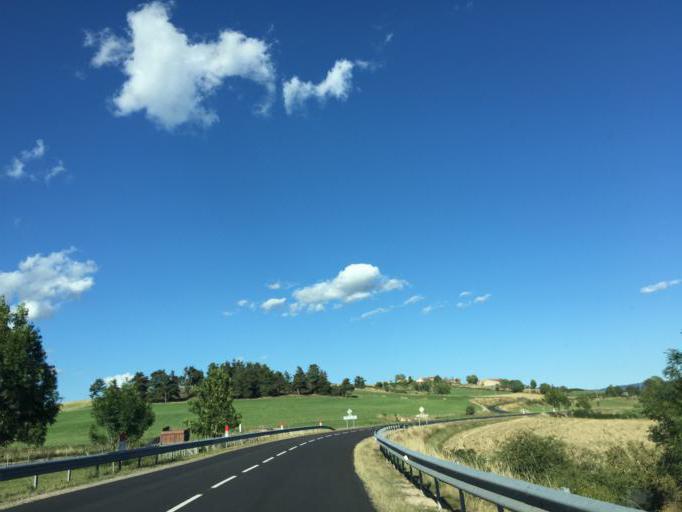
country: FR
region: Auvergne
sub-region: Departement de la Haute-Loire
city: Saugues
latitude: 44.9652
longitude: 3.5946
